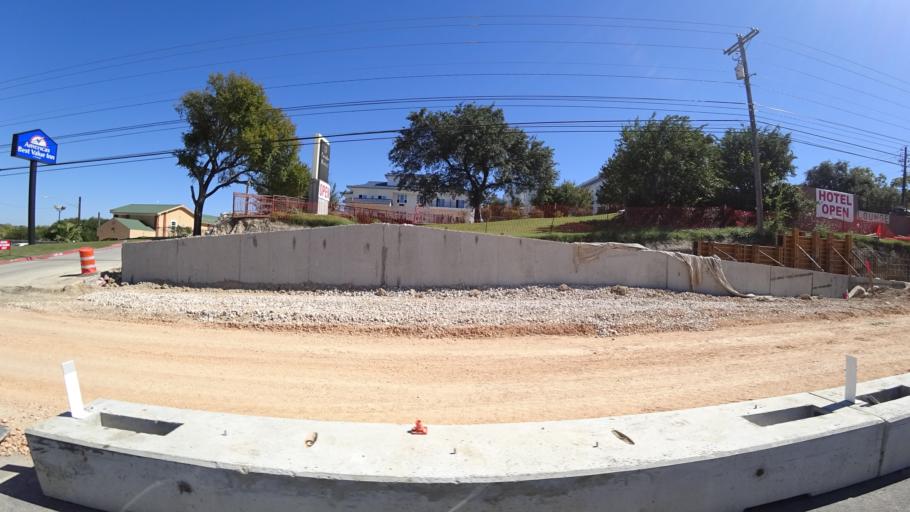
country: US
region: Texas
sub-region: Travis County
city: Austin
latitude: 30.2265
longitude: -97.7450
